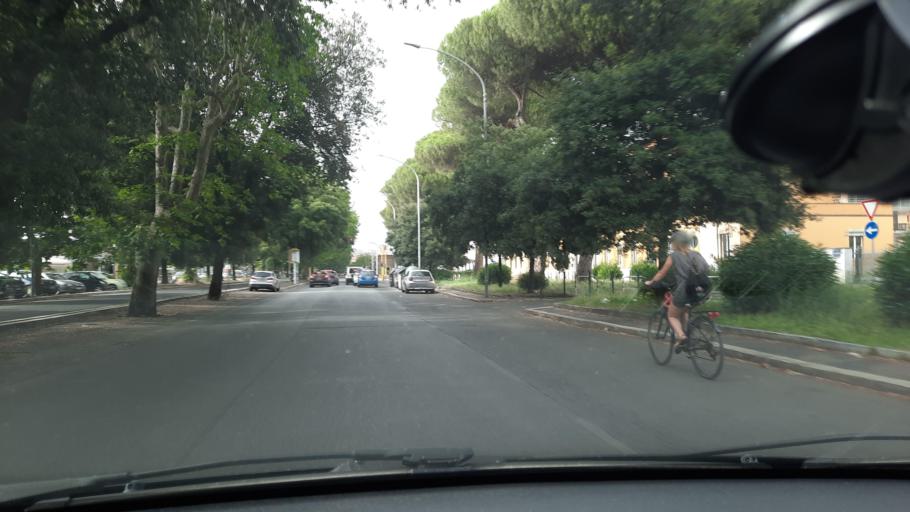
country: IT
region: Latium
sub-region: Citta metropolitana di Roma Capitale
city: Rome
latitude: 41.8618
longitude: 12.4785
